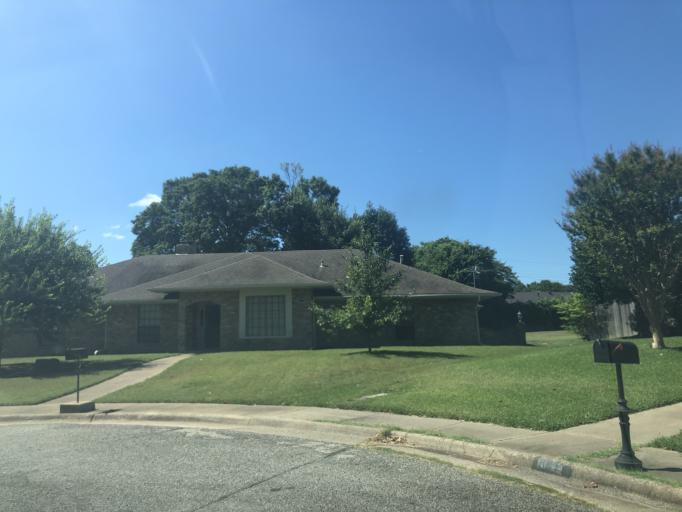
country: US
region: Texas
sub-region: Dallas County
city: Duncanville
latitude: 32.6421
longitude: -96.9284
